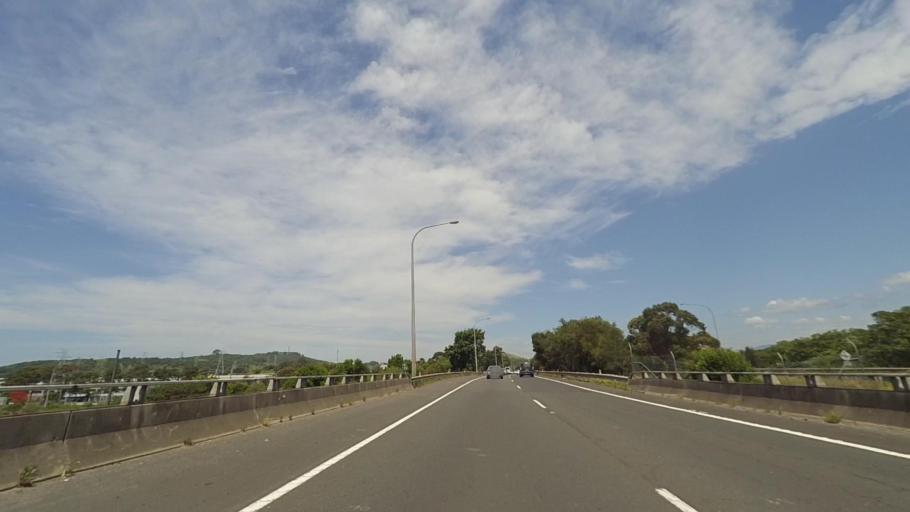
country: AU
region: New South Wales
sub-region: Wollongong
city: Mount Saint Thomas
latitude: -34.4538
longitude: 150.8586
